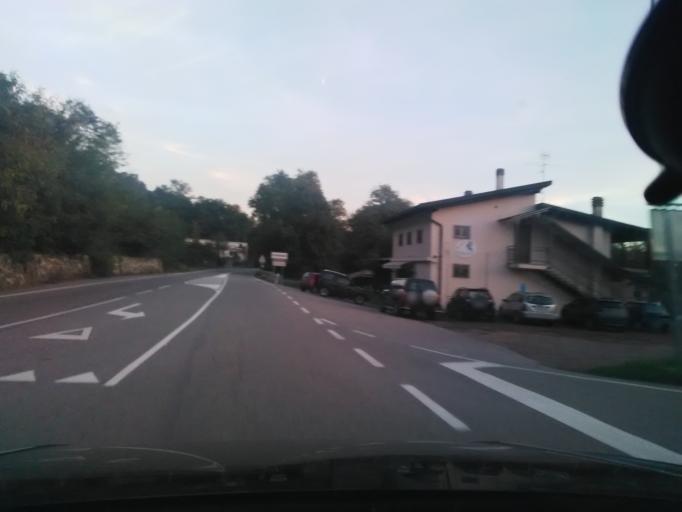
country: IT
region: Piedmont
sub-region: Provincia di Vercelli
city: Serravalle Sesia
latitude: 45.6912
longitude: 8.3191
